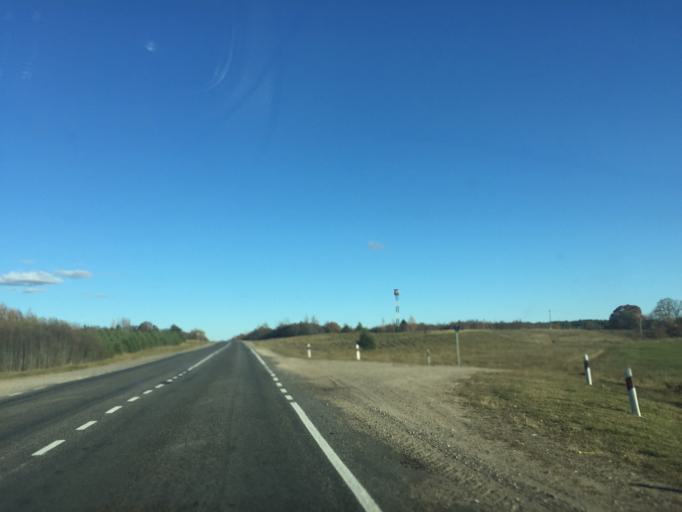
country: BY
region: Vitebsk
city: Dzisna
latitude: 55.2396
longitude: 28.0563
